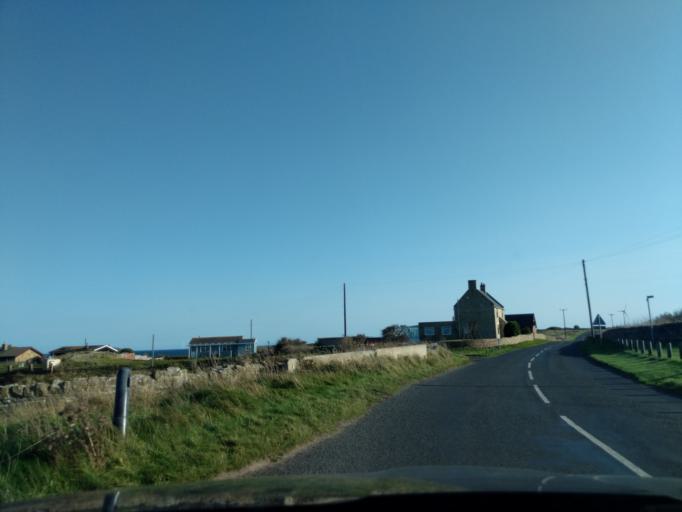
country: GB
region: England
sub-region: Northumberland
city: Lynemouth
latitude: 55.2286
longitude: -1.5292
